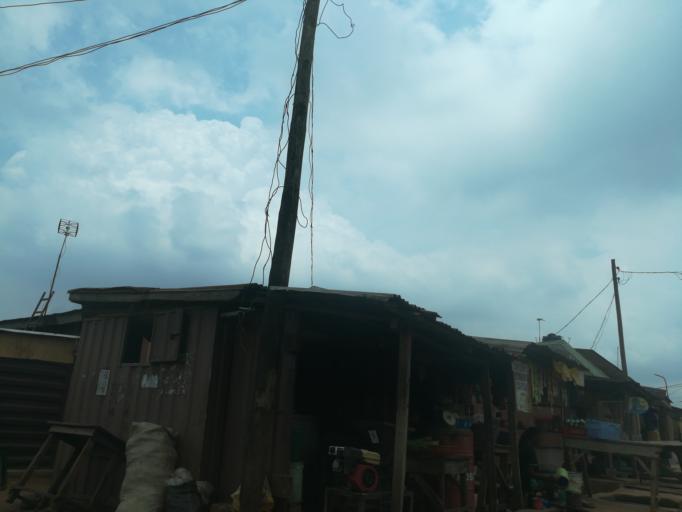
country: NG
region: Lagos
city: Ikorodu
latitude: 6.6192
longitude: 3.5218
